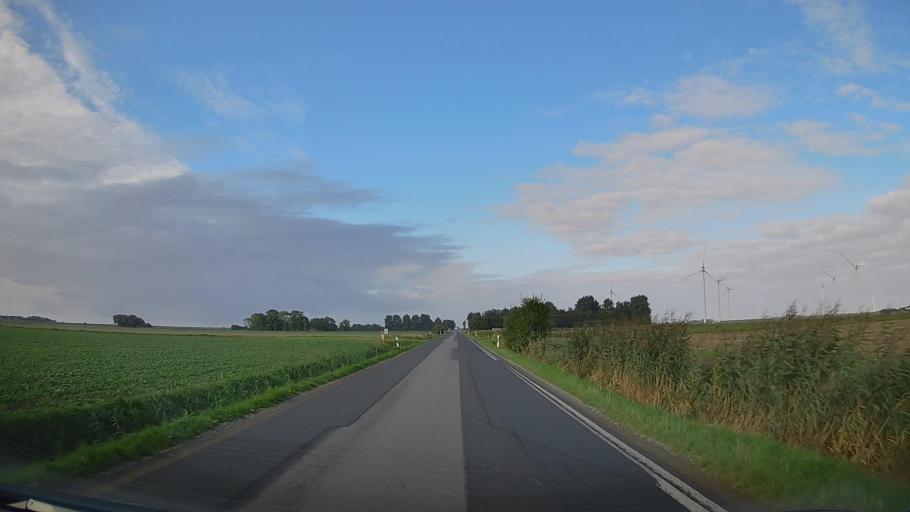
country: DE
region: Schleswig-Holstein
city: Breklum
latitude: 54.5733
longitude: 8.9613
